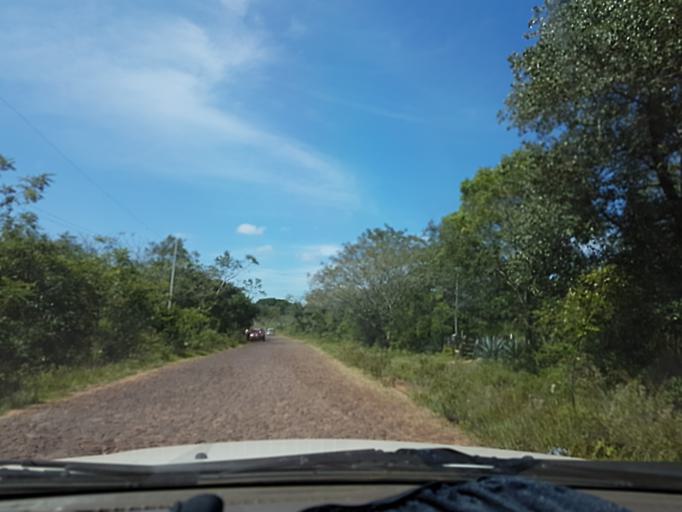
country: PY
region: Cordillera
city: Arroyos y Esteros
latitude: -24.9867
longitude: -57.2062
